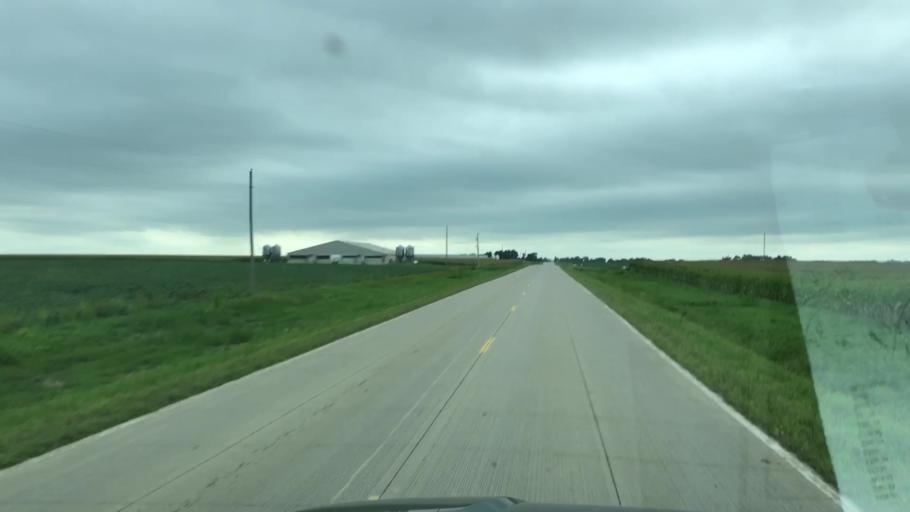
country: US
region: Iowa
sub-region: O'Brien County
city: Sheldon
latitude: 43.1296
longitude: -95.9791
